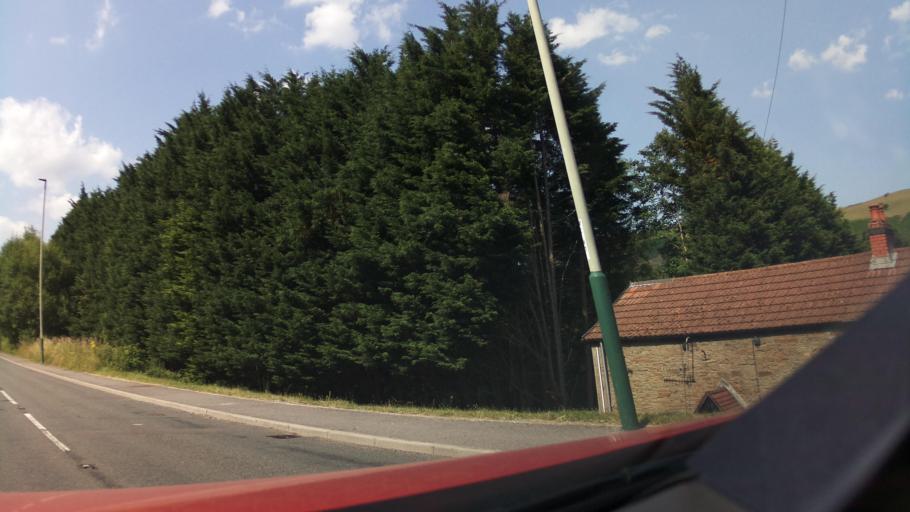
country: GB
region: Wales
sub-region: Caerphilly County Borough
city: New Tredegar
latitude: 51.7246
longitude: -3.2525
